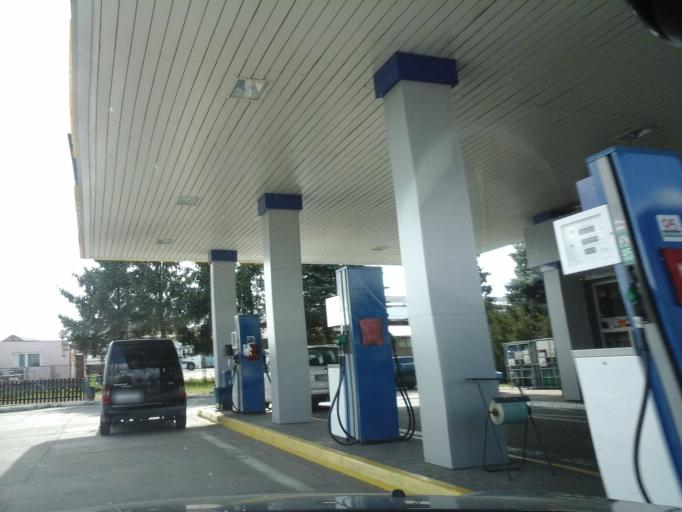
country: PL
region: West Pomeranian Voivodeship
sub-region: Powiat choszczenski
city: Choszczno
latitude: 53.1767
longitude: 15.4177
